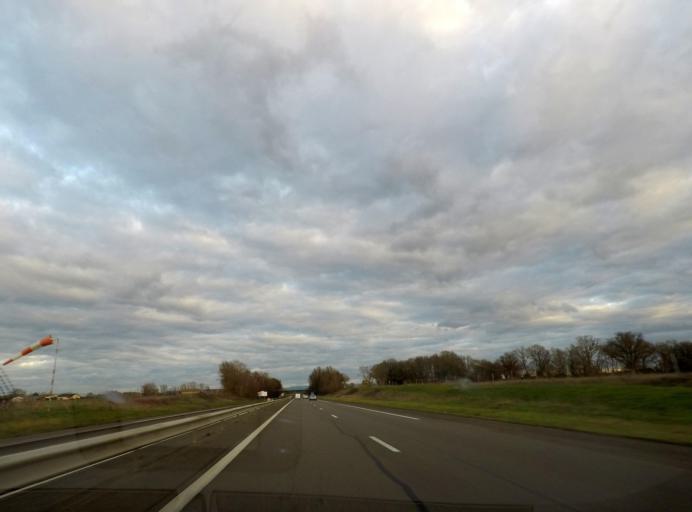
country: FR
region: Rhone-Alpes
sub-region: Departement de l'Ain
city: Saint-Cyr-sur-Menthon
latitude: 46.2817
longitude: 4.9641
